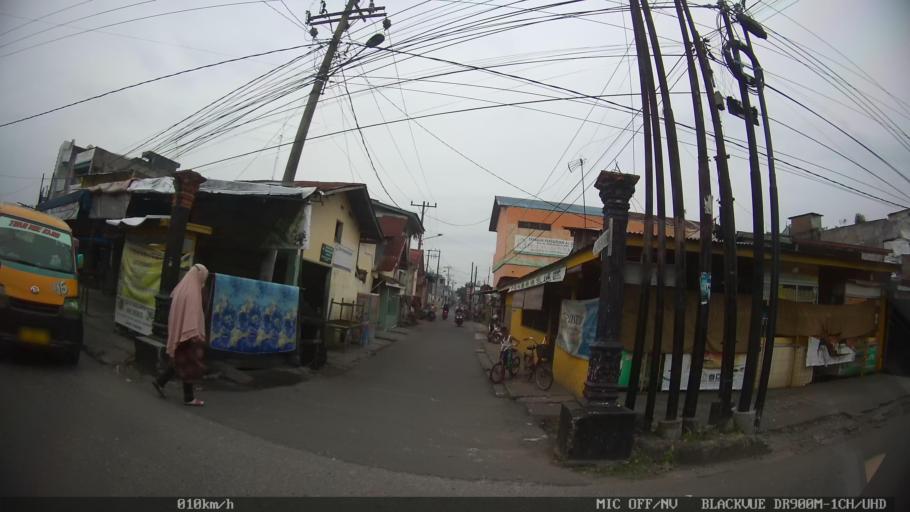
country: ID
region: North Sumatra
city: Medan
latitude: 3.5529
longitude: 98.6960
